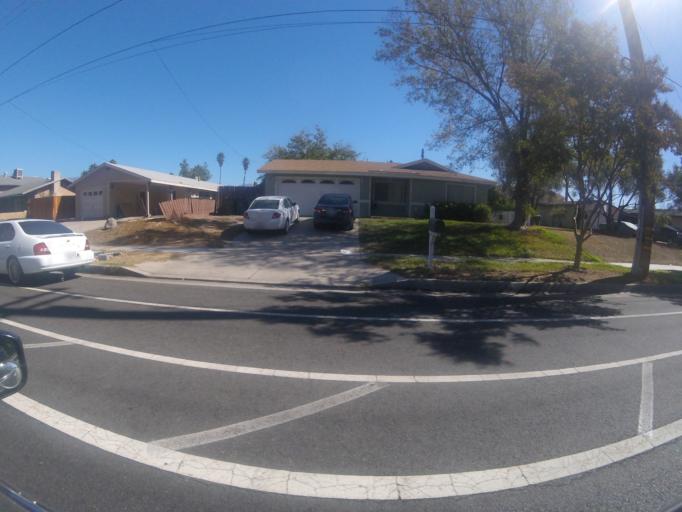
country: US
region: California
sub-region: San Bernardino County
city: Redlands
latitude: 34.0744
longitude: -117.1737
